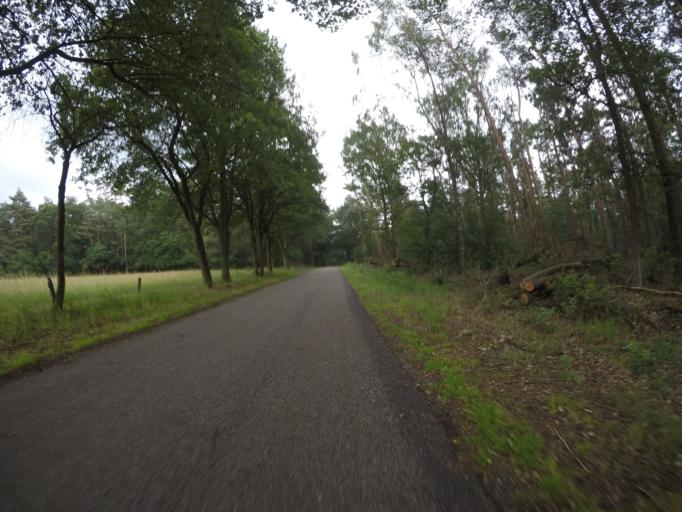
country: DE
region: North Rhine-Westphalia
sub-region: Regierungsbezirk Dusseldorf
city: Hunxe
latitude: 51.6383
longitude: 6.7972
